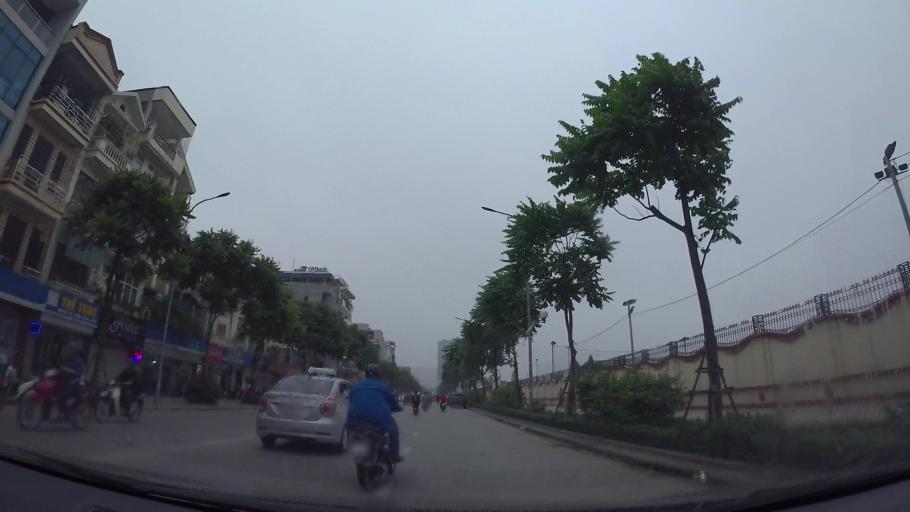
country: VN
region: Ha Noi
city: Hai BaTrung
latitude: 20.9934
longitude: 105.8317
